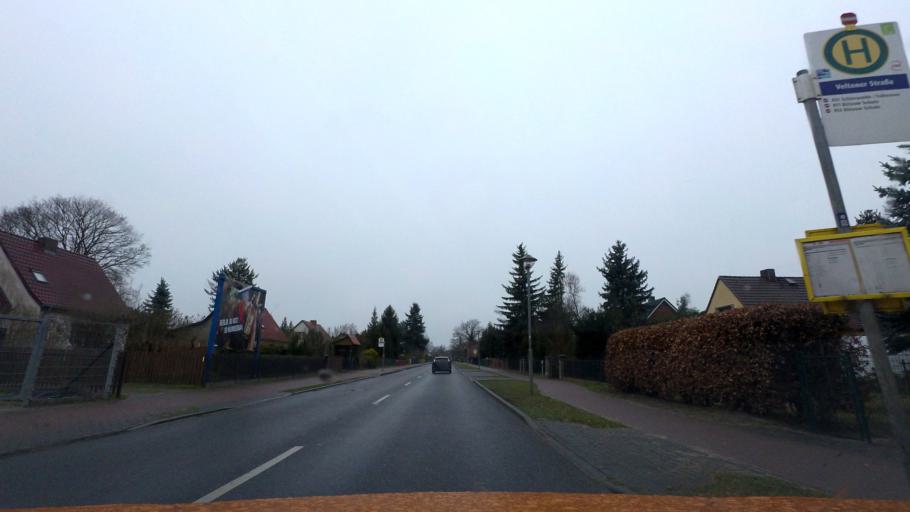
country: DE
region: Brandenburg
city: Velten
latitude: 52.6552
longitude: 13.1449
